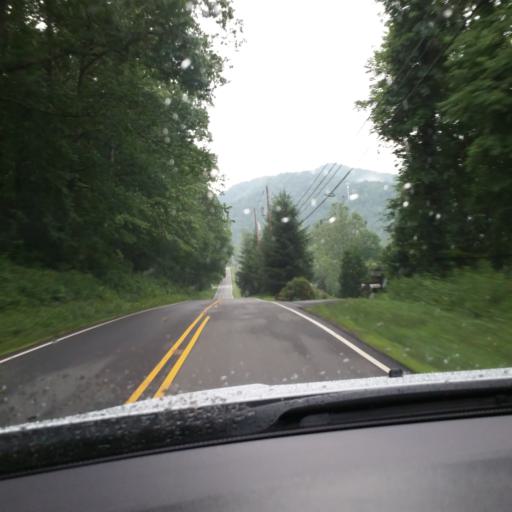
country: US
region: North Carolina
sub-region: Yancey County
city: Burnsville
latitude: 35.7794
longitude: -82.2001
